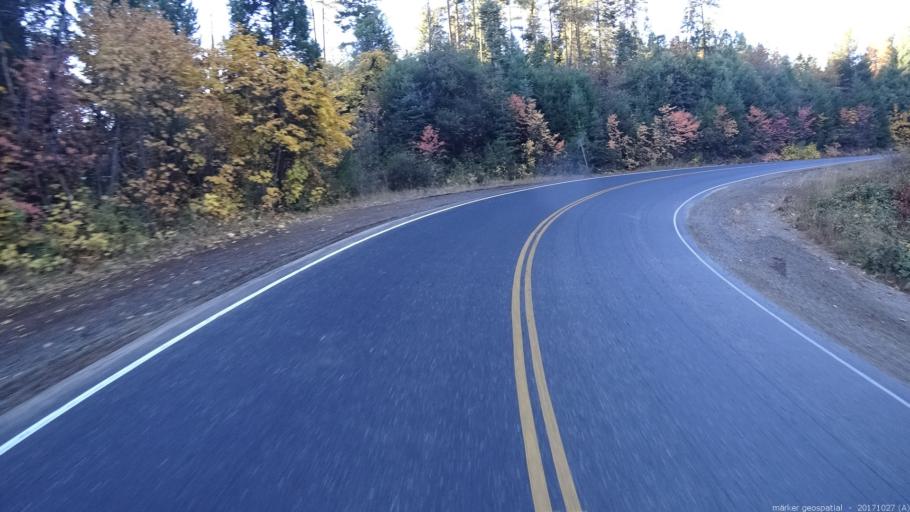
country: US
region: California
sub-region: Shasta County
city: Burney
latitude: 40.8866
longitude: -121.9065
